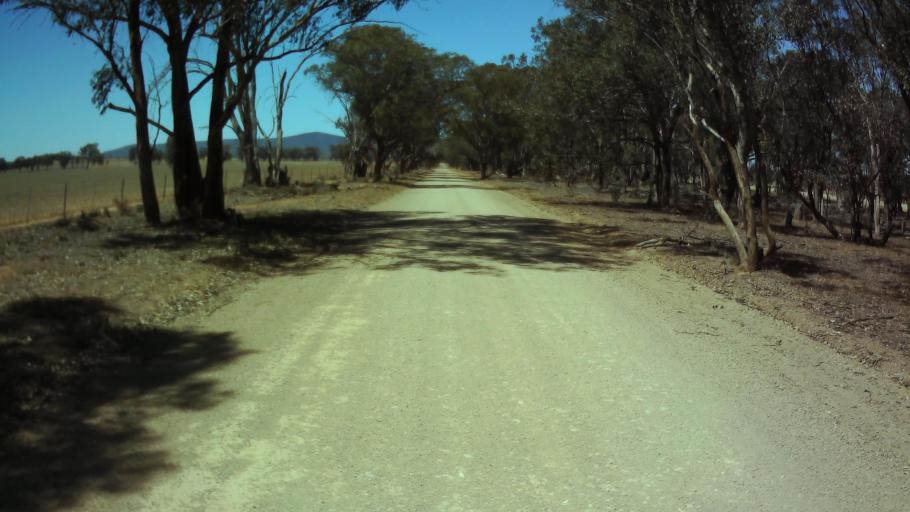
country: AU
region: New South Wales
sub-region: Weddin
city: Grenfell
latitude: -33.8968
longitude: 148.0843
